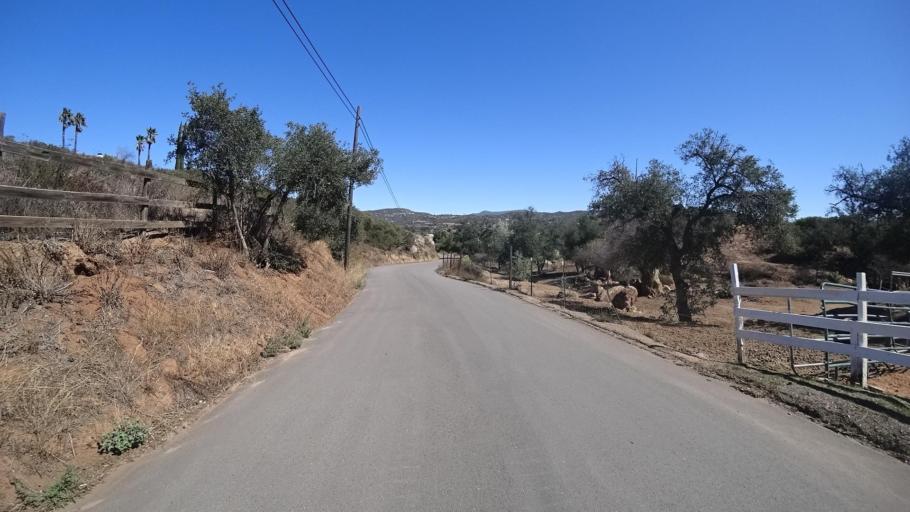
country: US
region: California
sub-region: San Diego County
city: Alpine
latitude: 32.7646
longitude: -116.6945
